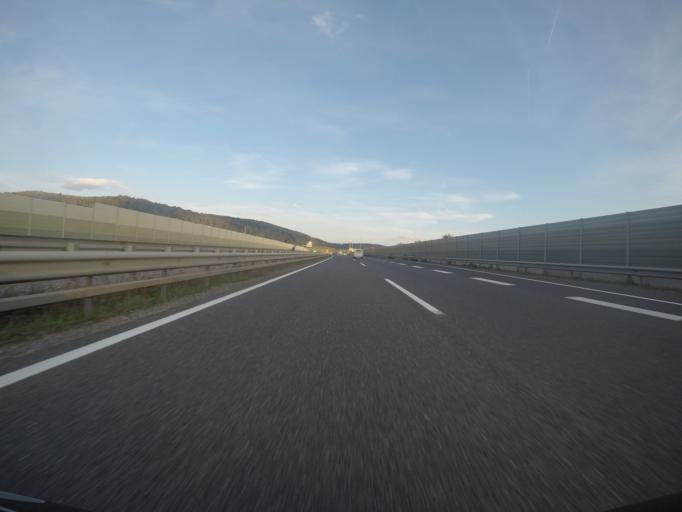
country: SI
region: Grosuplje
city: Smarje-Sap
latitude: 45.9757
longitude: 14.6193
